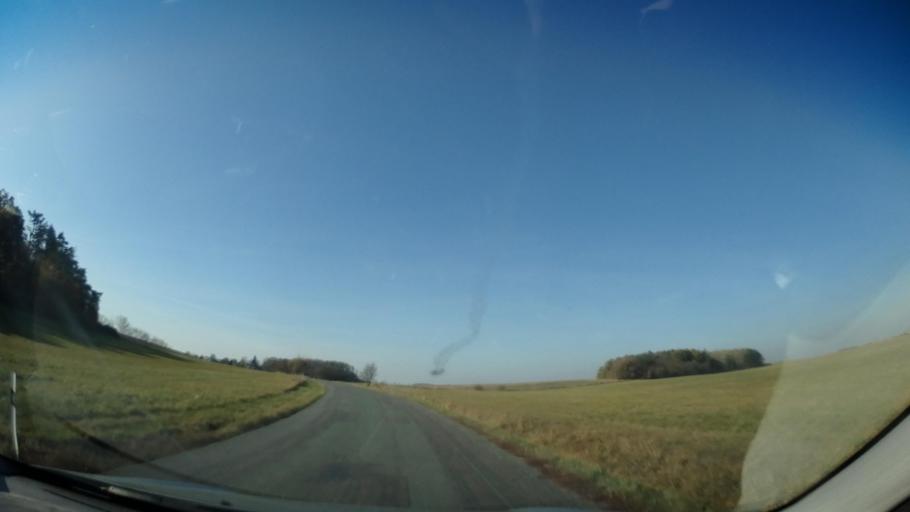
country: CZ
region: Kralovehradecky
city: Dolni Cernilov
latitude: 50.2488
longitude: 16.0043
